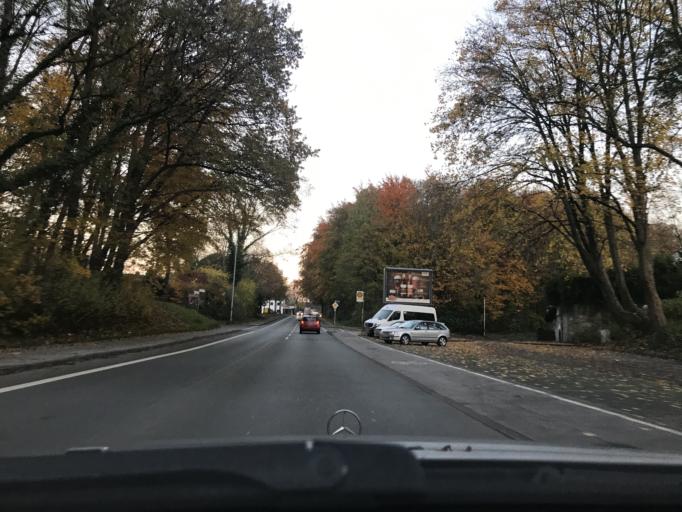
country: DE
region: North Rhine-Westphalia
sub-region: Regierungsbezirk Arnsberg
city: Soest
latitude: 51.5555
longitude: 8.1175
